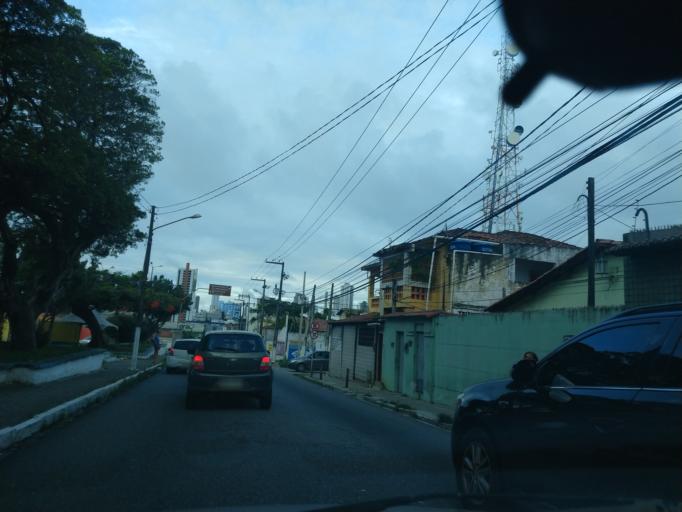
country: BR
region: Rio Grande do Norte
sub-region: Natal
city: Natal
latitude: -5.7928
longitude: -35.2124
